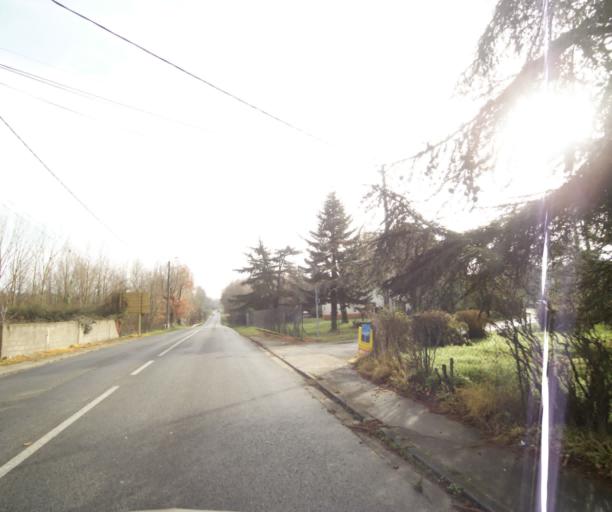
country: FR
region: Midi-Pyrenees
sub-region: Departement de la Haute-Garonne
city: Villemur-sur-Tarn
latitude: 43.8587
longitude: 1.4837
